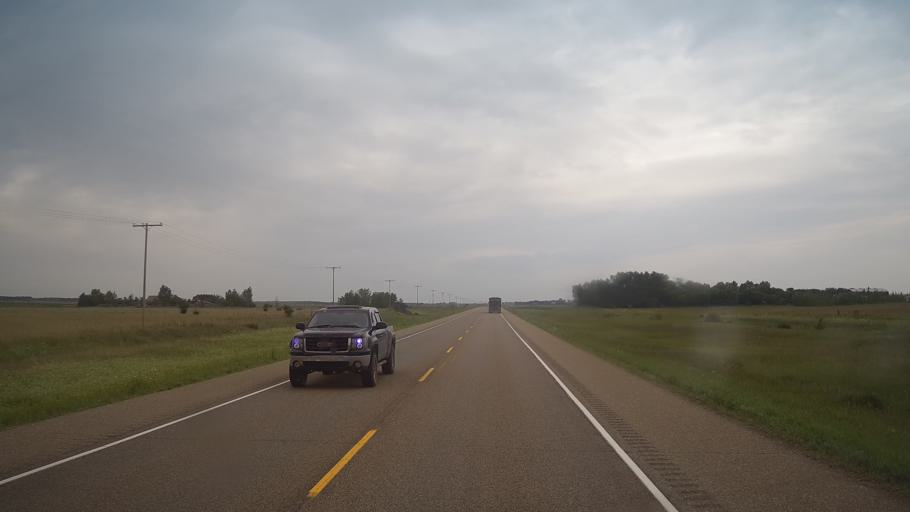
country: CA
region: Saskatchewan
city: Langham
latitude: 52.1289
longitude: -107.1380
